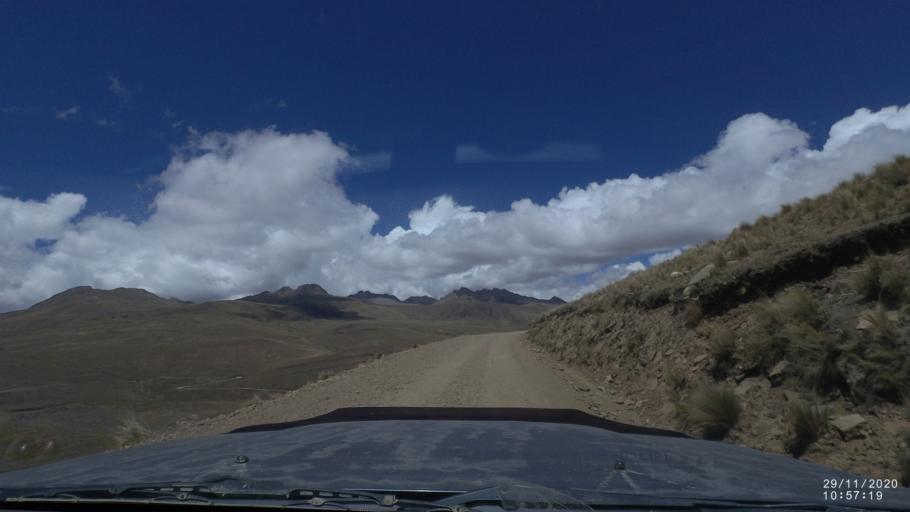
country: BO
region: Cochabamba
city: Cochabamba
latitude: -17.2153
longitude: -66.2278
